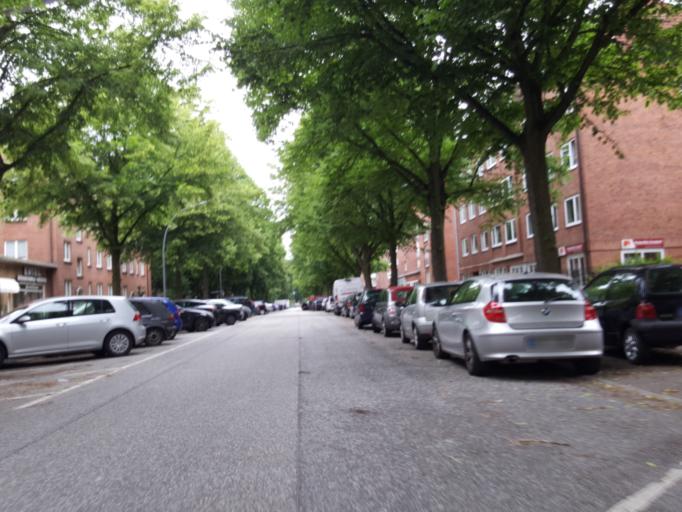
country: DE
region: Hamburg
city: Marienthal
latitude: 53.5548
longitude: 10.0790
